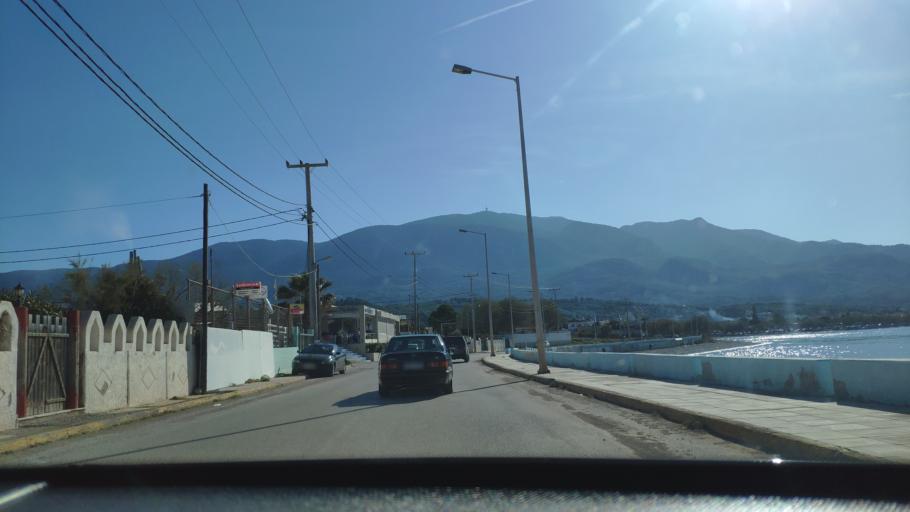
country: GR
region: Attica
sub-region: Nomarchia Dytikis Attikis
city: Kineta
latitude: 38.0766
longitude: 23.1736
